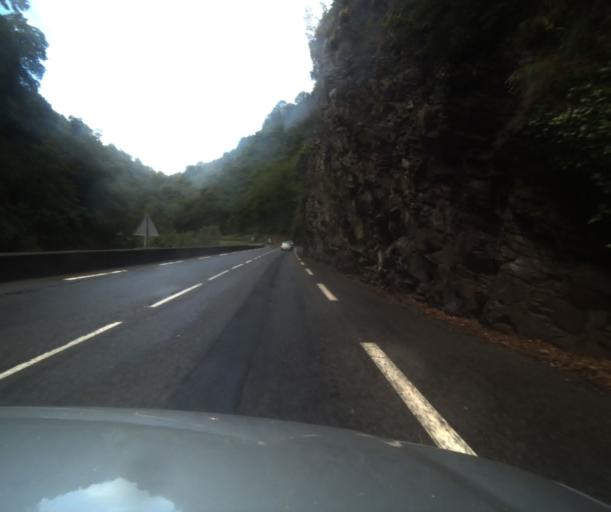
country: FR
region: Midi-Pyrenees
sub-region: Departement des Hautes-Pyrenees
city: Pierrefitte-Nestalas
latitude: 42.9381
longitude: -0.0499
